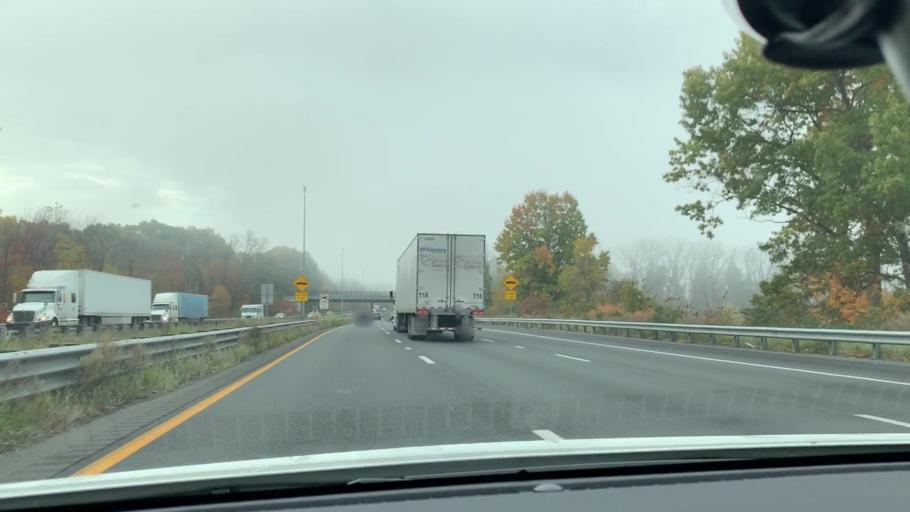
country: US
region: Massachusetts
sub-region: Hampden County
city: Longmeadow
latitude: 42.0392
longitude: -72.5887
